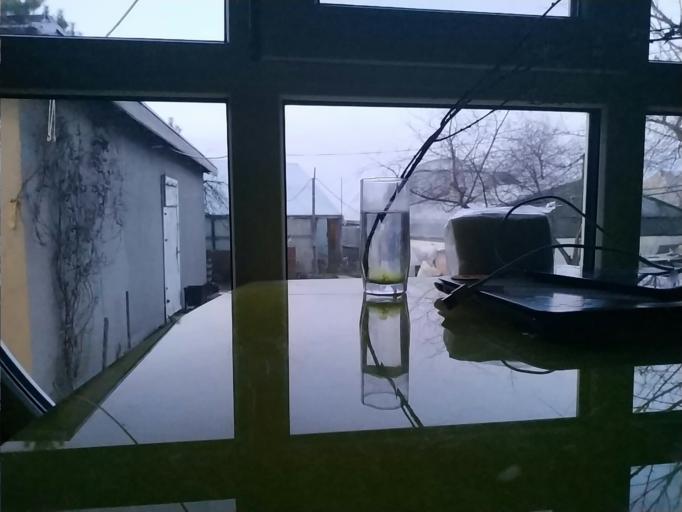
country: RU
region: Republic of Karelia
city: Sukkozero
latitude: 62.7539
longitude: 31.8651
